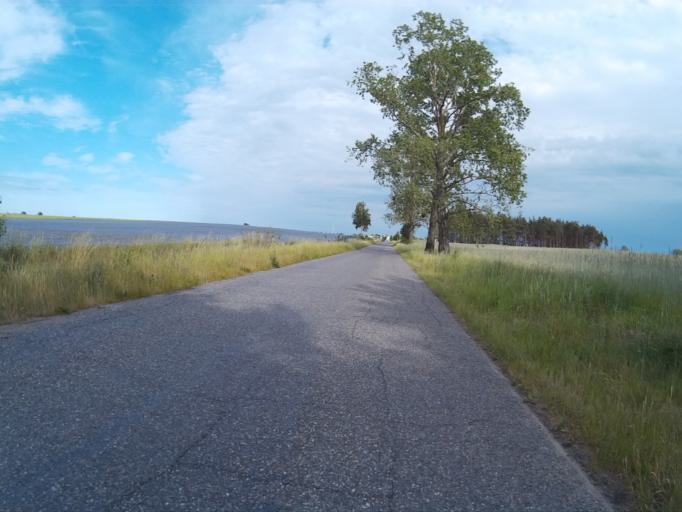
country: PL
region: Kujawsko-Pomorskie
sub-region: Powiat tucholski
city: Lubiewo
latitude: 53.4687
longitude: 17.9967
